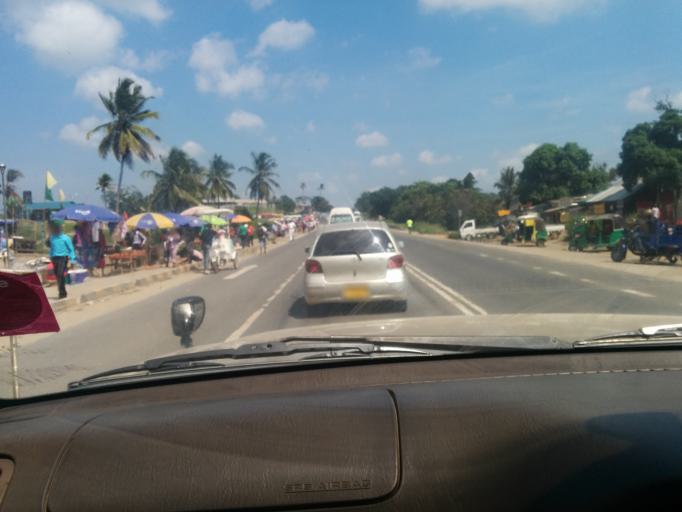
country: TZ
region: Pwani
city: Kisarawe
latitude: -6.7852
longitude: 39.1139
